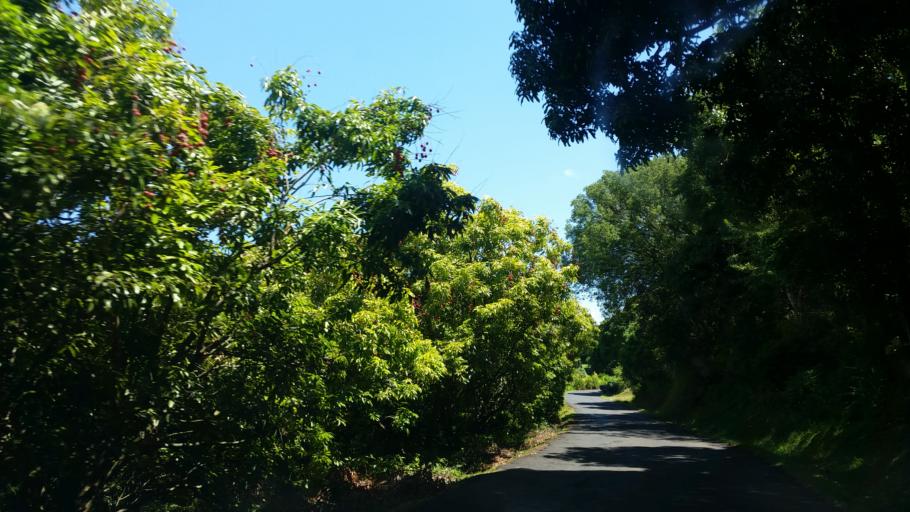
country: RE
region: Reunion
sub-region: Reunion
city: Sainte-Marie
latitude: -20.9324
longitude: 55.5289
